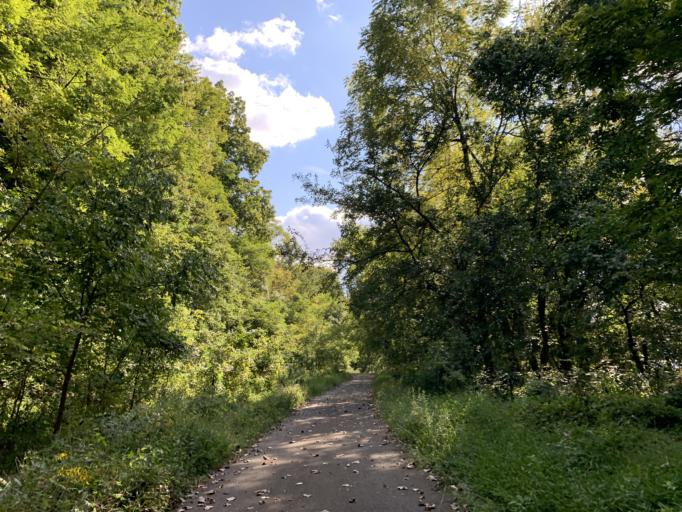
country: US
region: Indiana
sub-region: Floyd County
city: New Albany
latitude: 38.2593
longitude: -85.8317
